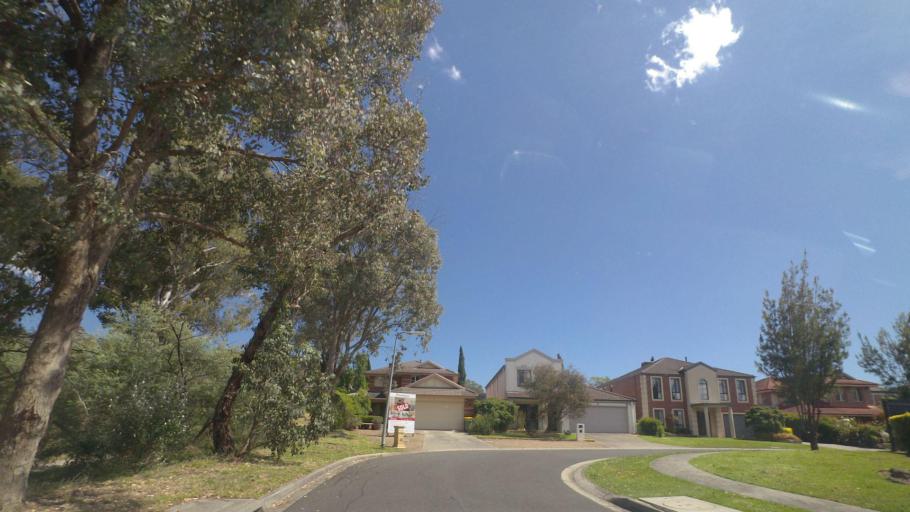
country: AU
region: Victoria
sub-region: Yarra Ranges
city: Kilsyth
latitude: -37.8062
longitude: 145.3282
